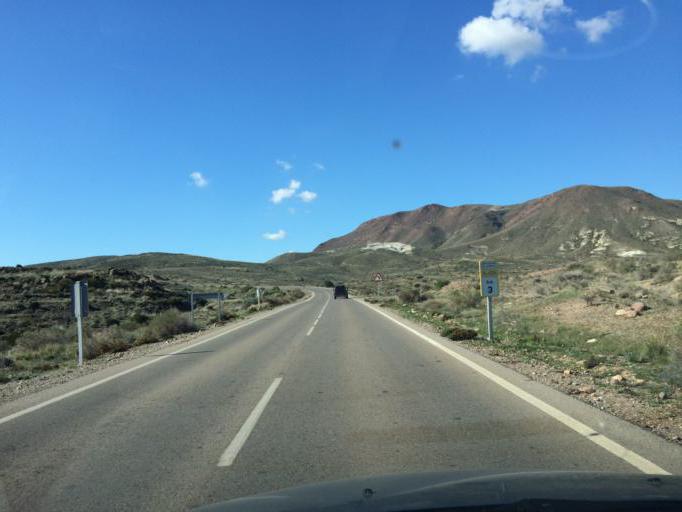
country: ES
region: Andalusia
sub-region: Provincia de Almeria
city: San Jose
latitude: 36.8070
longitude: -2.0849
